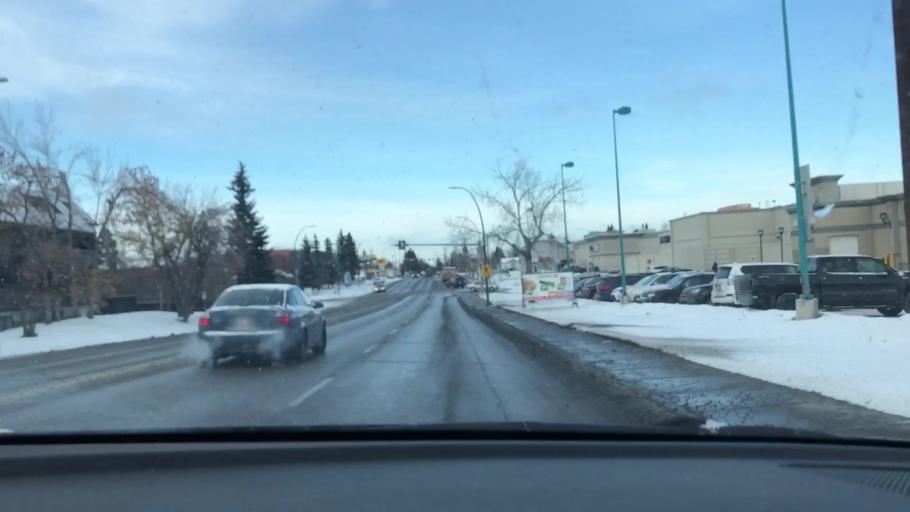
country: CA
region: Alberta
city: Calgary
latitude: 51.0422
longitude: -114.1411
